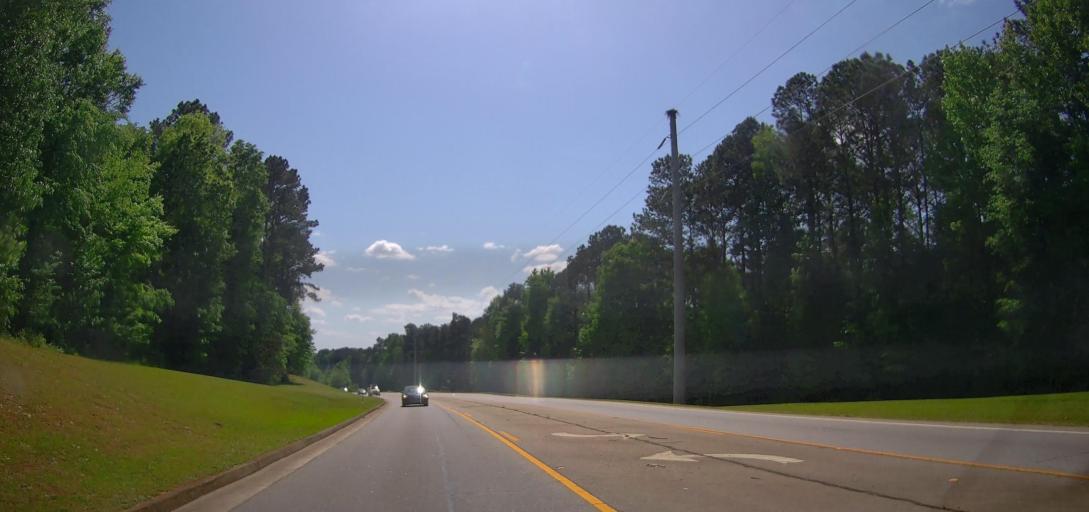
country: US
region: Georgia
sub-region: Putnam County
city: Jefferson
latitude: 33.4538
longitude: -83.2506
